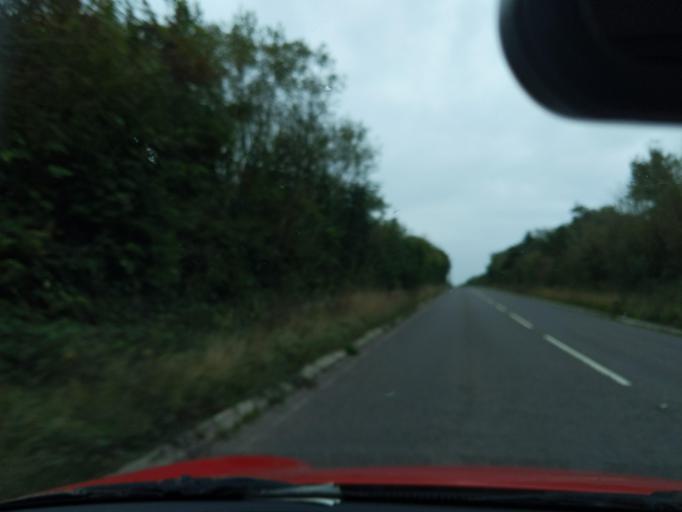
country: GB
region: England
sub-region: Devon
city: Okehampton
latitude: 50.8256
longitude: -4.0759
